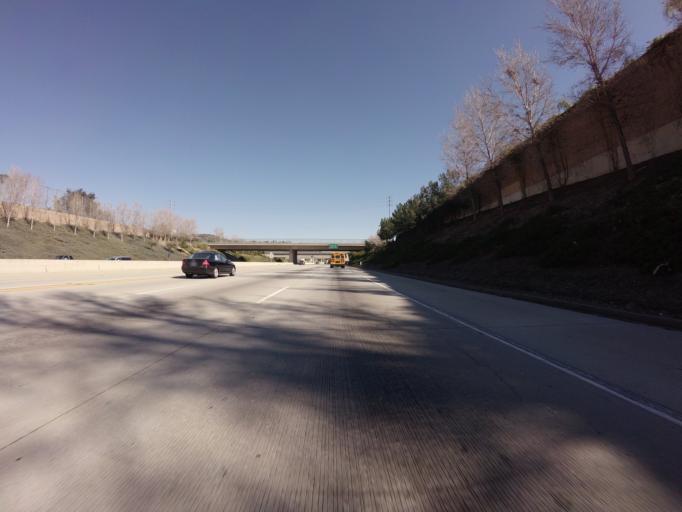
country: US
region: California
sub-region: Los Angeles County
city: Claremont
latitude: 34.1201
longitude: -117.7121
